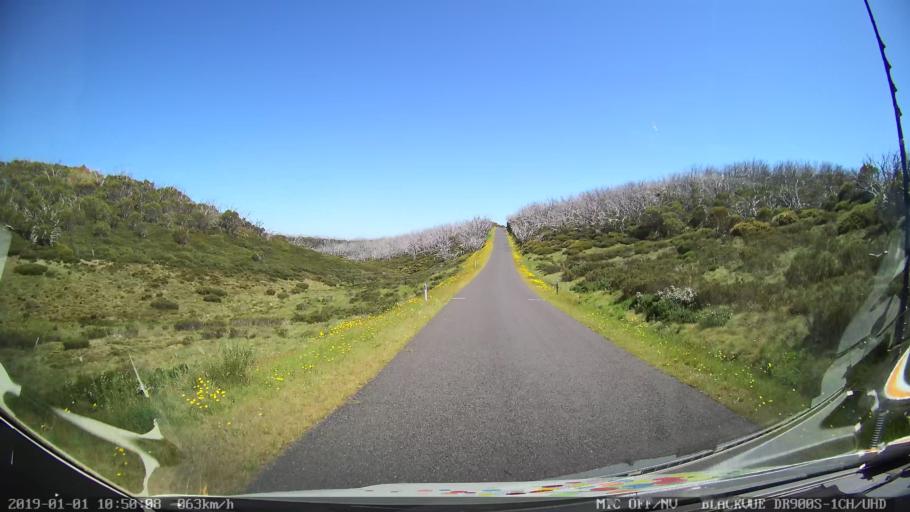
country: AU
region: New South Wales
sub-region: Snowy River
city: Jindabyne
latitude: -36.0310
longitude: 148.3730
